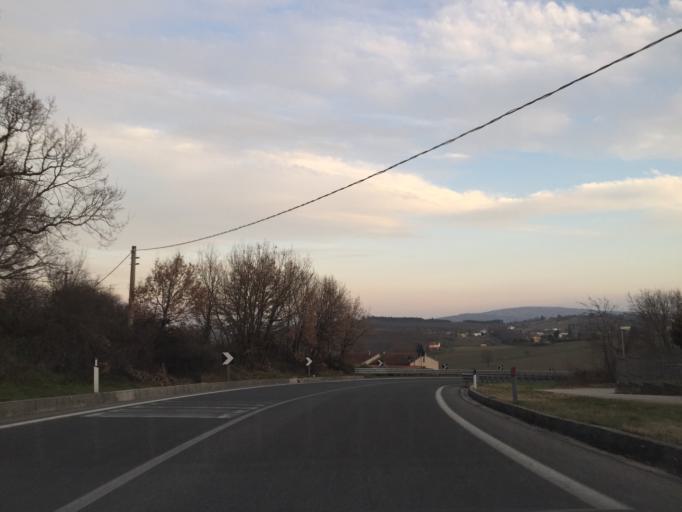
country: IT
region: Molise
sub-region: Provincia di Campobasso
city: Campobasso
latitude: 41.5605
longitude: 14.7004
